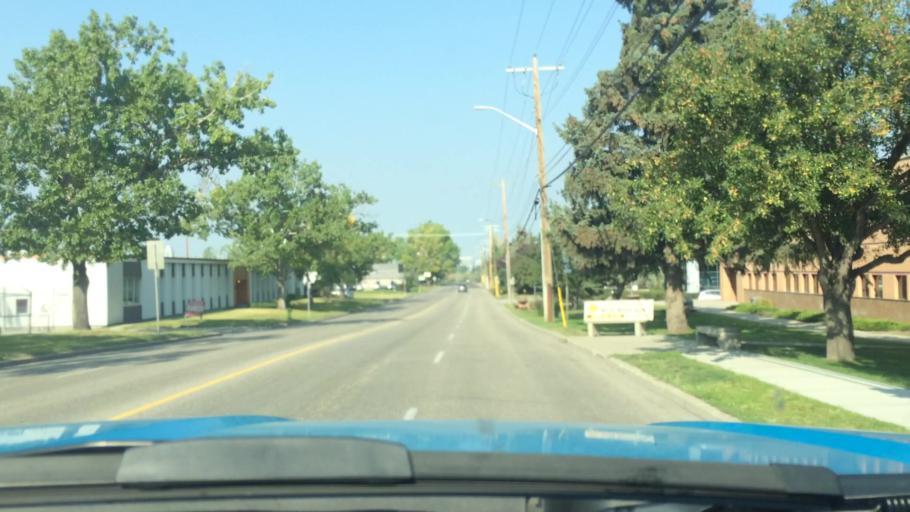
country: CA
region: Alberta
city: Calgary
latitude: 51.0525
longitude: -114.0090
